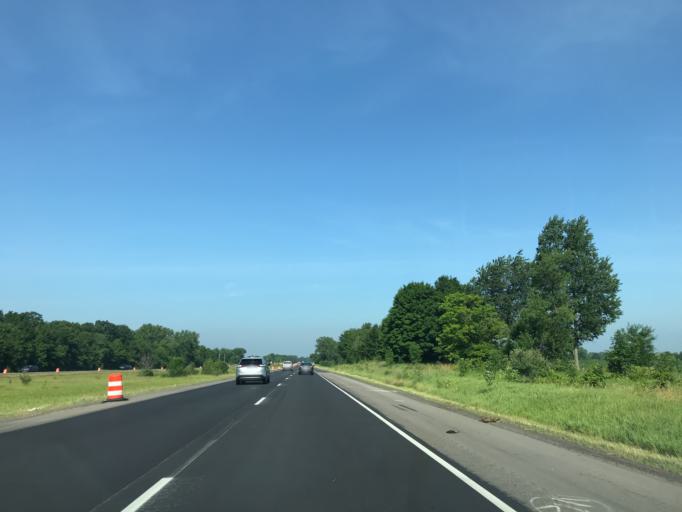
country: US
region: Michigan
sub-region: Ingham County
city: Webberville
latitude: 42.6515
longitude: -84.1534
